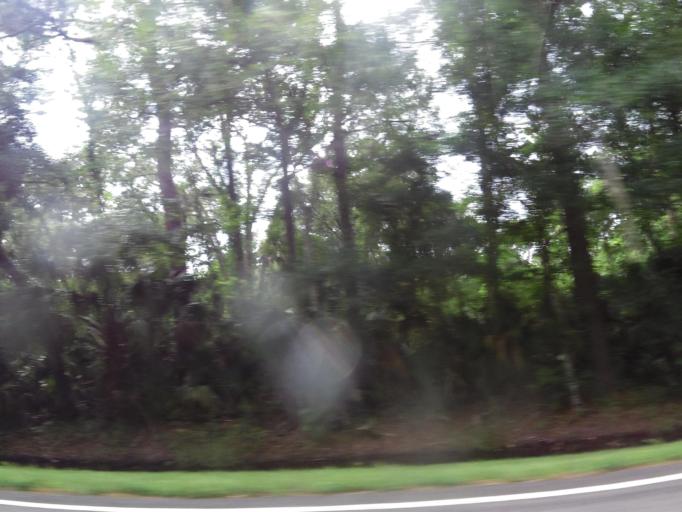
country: US
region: Florida
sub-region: Saint Johns County
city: Saint Augustine
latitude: 29.8702
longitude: -81.3717
